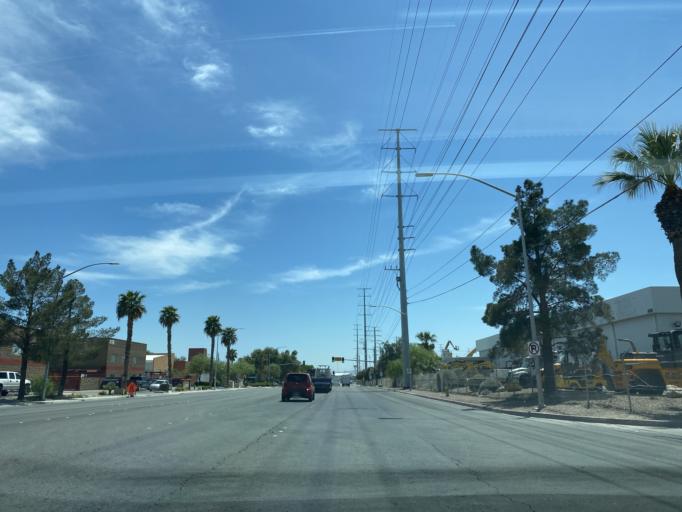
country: US
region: Nevada
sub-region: Clark County
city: North Las Vegas
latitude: 36.2361
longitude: -115.1168
